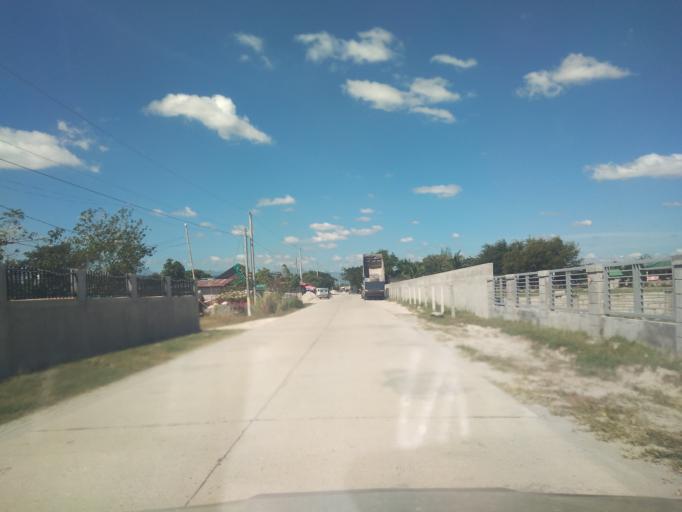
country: PH
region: Central Luzon
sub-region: Province of Pampanga
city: Balas
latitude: 15.0573
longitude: 120.5994
